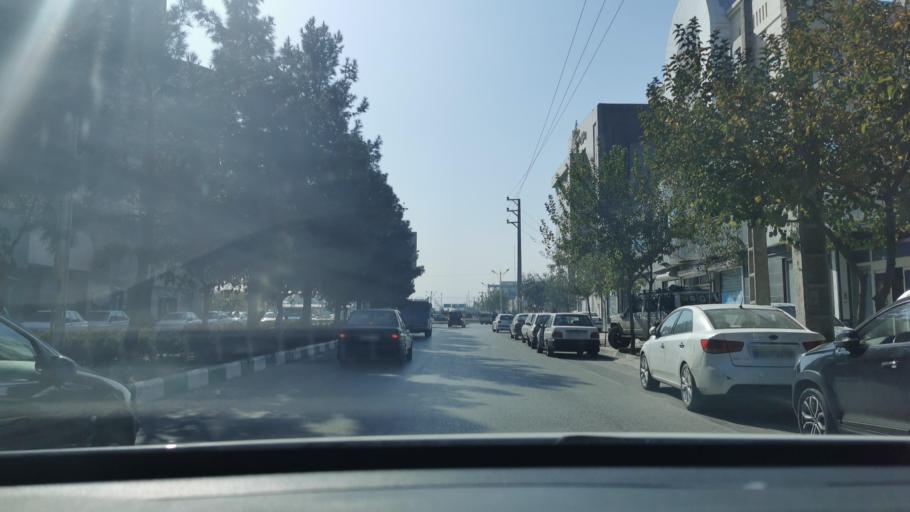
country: IR
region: Razavi Khorasan
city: Mashhad
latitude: 36.3482
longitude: 59.5953
